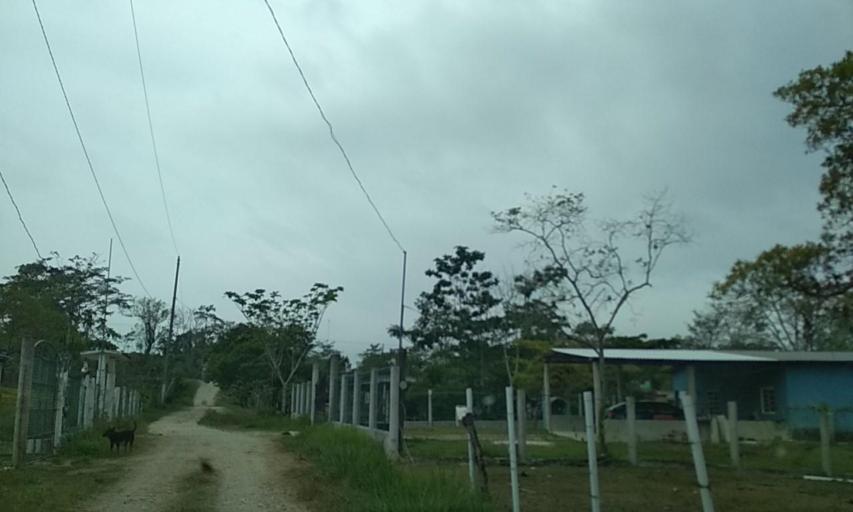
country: MX
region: Tabasco
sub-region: Huimanguillo
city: Francisco Rueda
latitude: 17.5692
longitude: -94.1093
